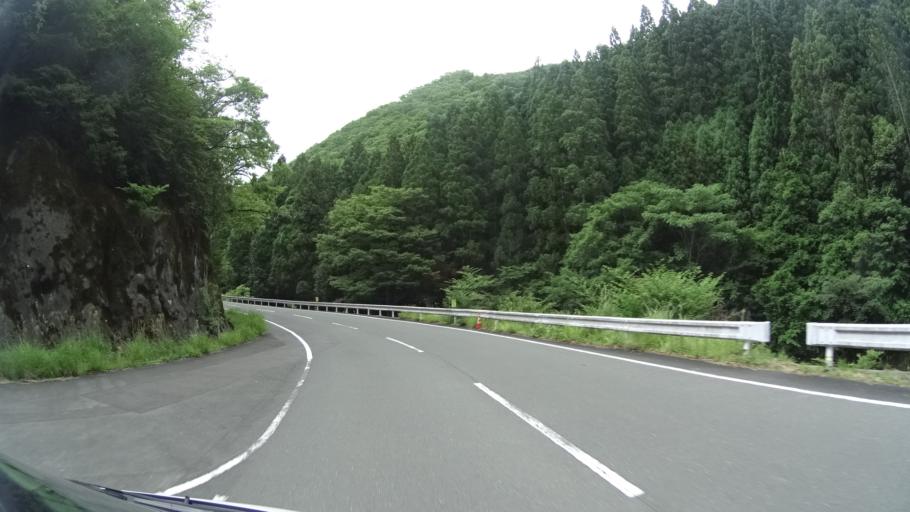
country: JP
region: Hyogo
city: Sasayama
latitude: 35.0625
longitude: 135.3949
